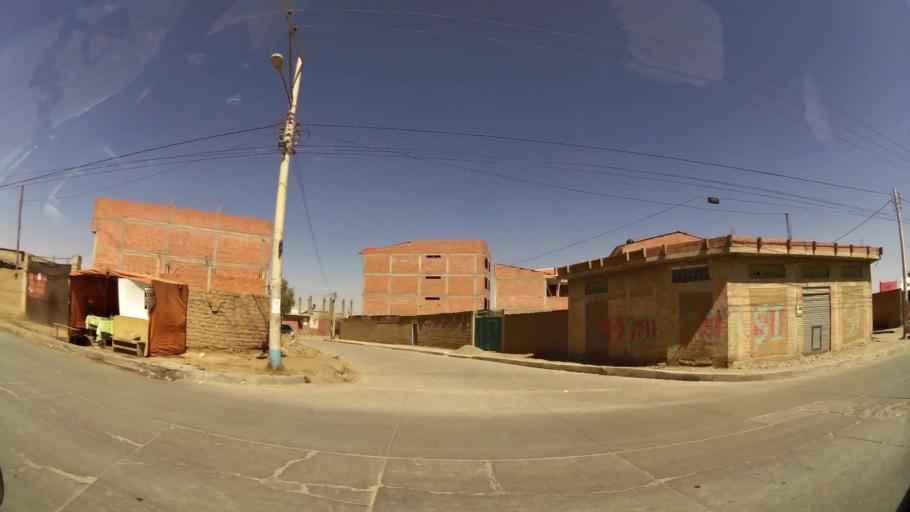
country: BO
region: La Paz
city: La Paz
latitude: -16.5521
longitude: -68.1863
